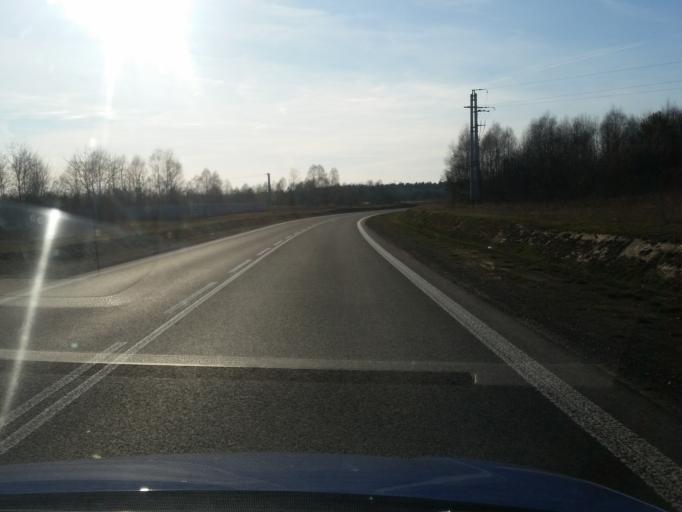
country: PL
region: Lodz Voivodeship
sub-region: Powiat radomszczanski
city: Radomsko
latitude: 51.1067
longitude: 19.4568
